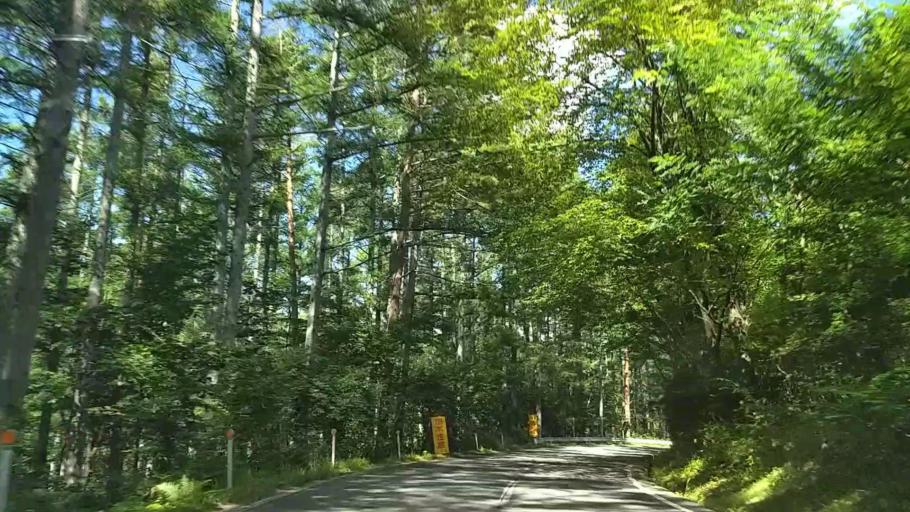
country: JP
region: Nagano
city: Matsumoto
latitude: 36.1975
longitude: 138.0679
